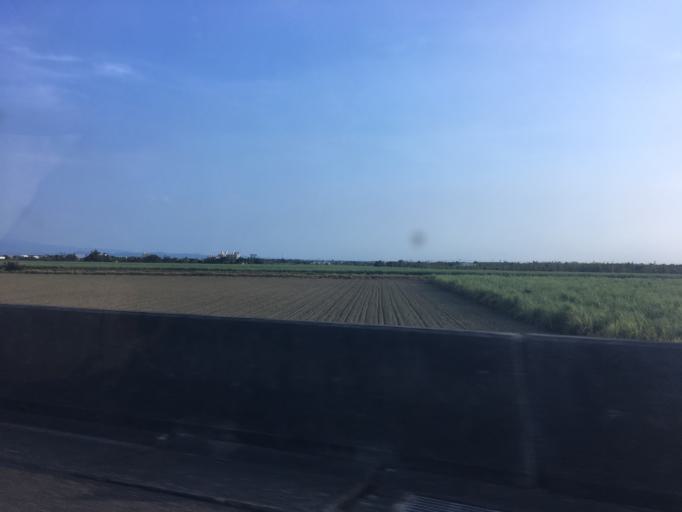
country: TW
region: Taiwan
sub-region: Chiayi
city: Taibao
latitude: 23.4258
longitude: 120.3503
